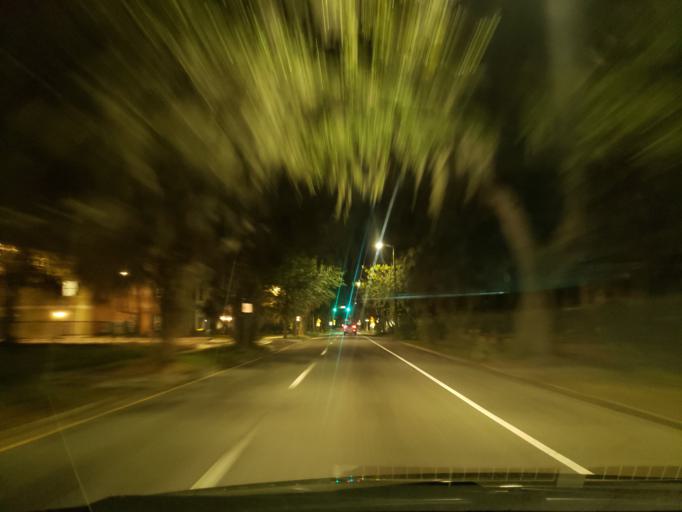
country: US
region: Georgia
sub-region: Chatham County
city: Savannah
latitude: 32.0586
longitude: -81.0803
